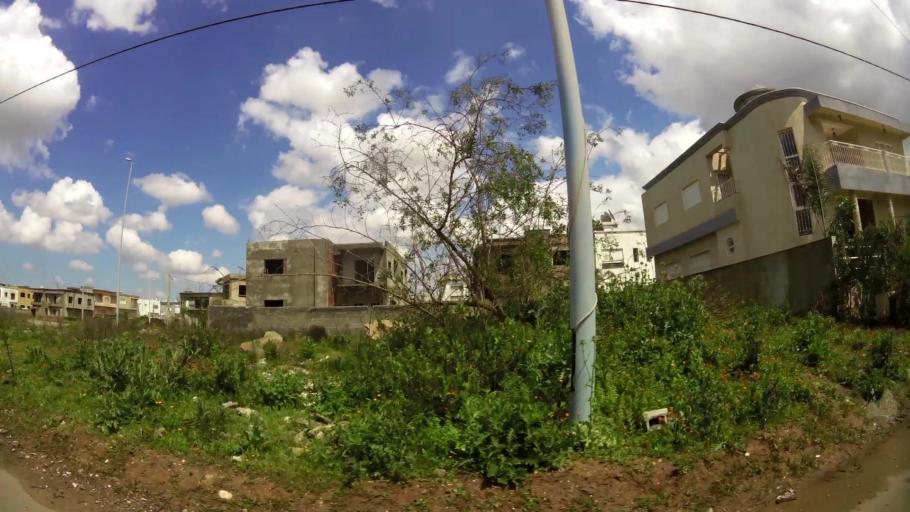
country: MA
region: Chaouia-Ouardigha
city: Nouaseur
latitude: 33.3953
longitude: -7.5628
